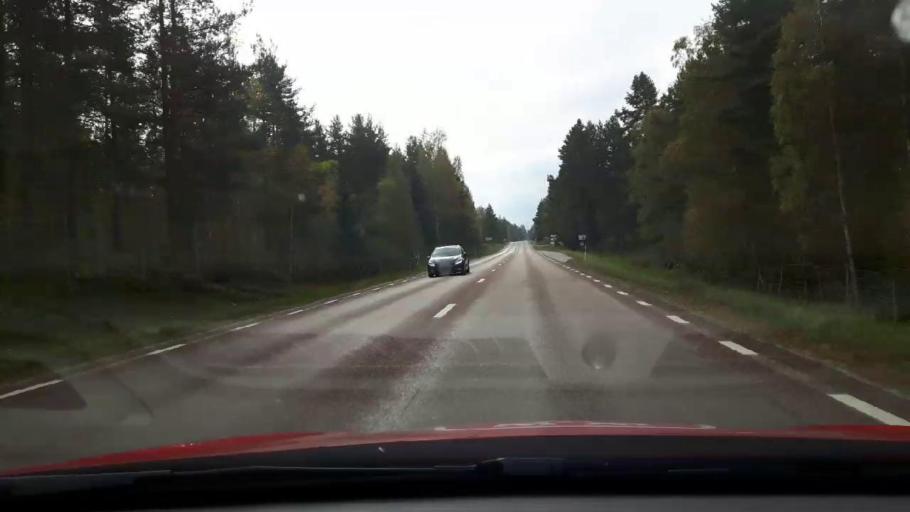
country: SE
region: Gaevleborg
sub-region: Bollnas Kommun
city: Kilafors
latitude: 61.2571
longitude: 16.5525
